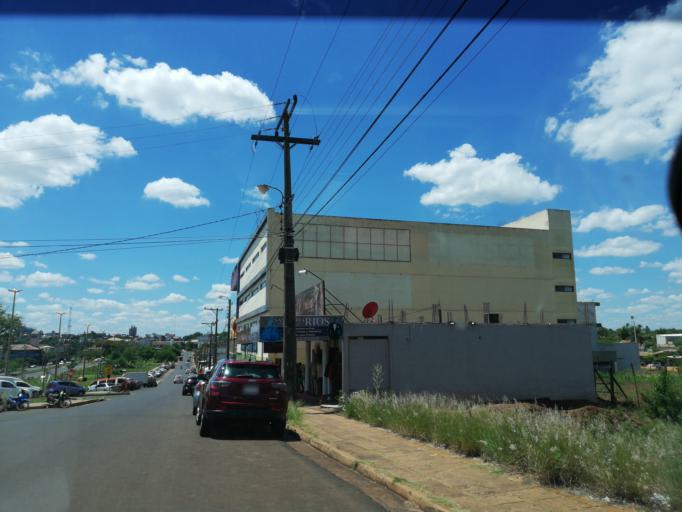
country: PY
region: Itapua
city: Encarnacion
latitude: -27.3525
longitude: -55.8581
